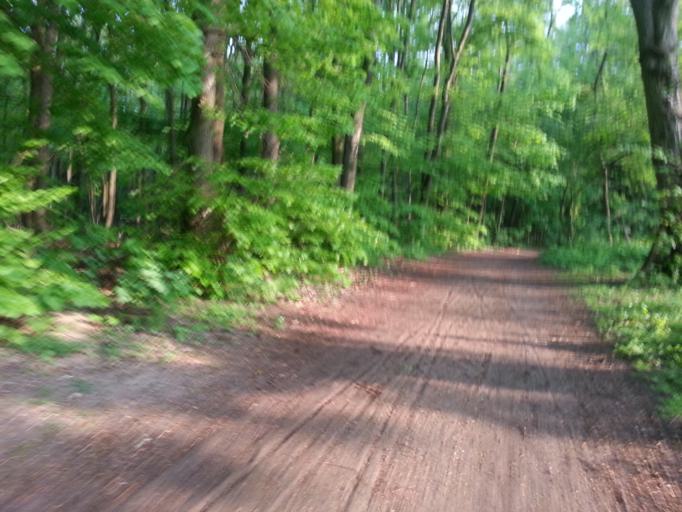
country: DE
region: Berlin
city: Siemensstadt
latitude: 52.5673
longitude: 13.2561
